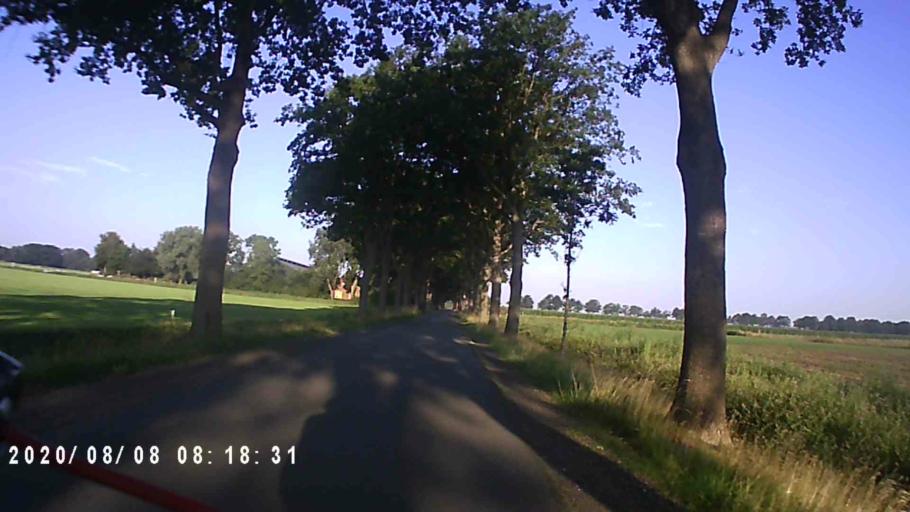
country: NL
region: Groningen
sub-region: Gemeente Leek
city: Leek
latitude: 53.0964
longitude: 6.3227
